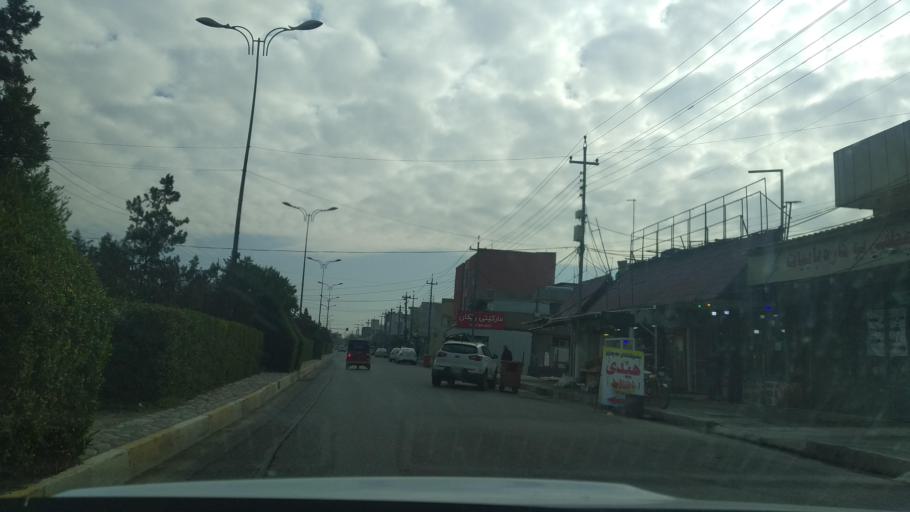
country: IQ
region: Arbil
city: Erbil
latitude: 36.1772
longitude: 44.0297
